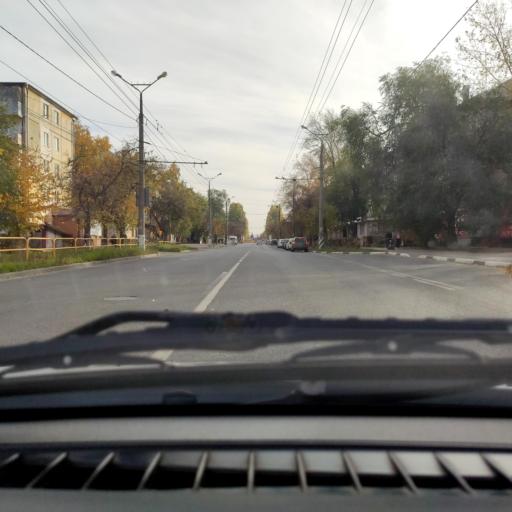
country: RU
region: Samara
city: Tol'yatti
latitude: 53.5138
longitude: 49.4176
